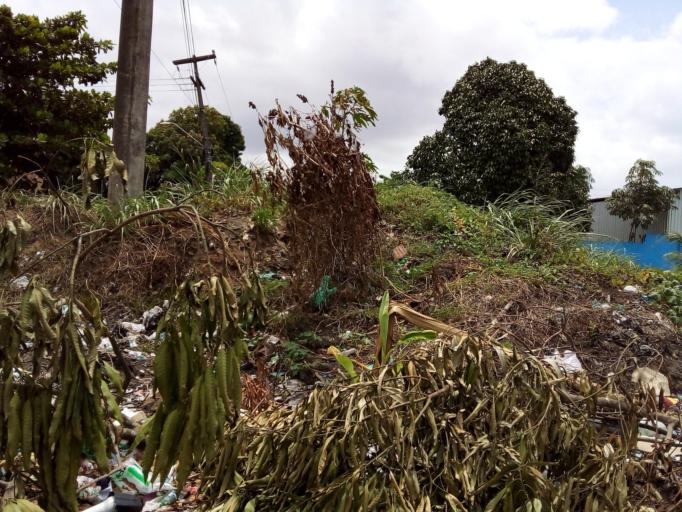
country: BR
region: Maranhao
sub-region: Sao Luis
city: Sao Luis
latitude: -2.6905
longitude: -44.3029
